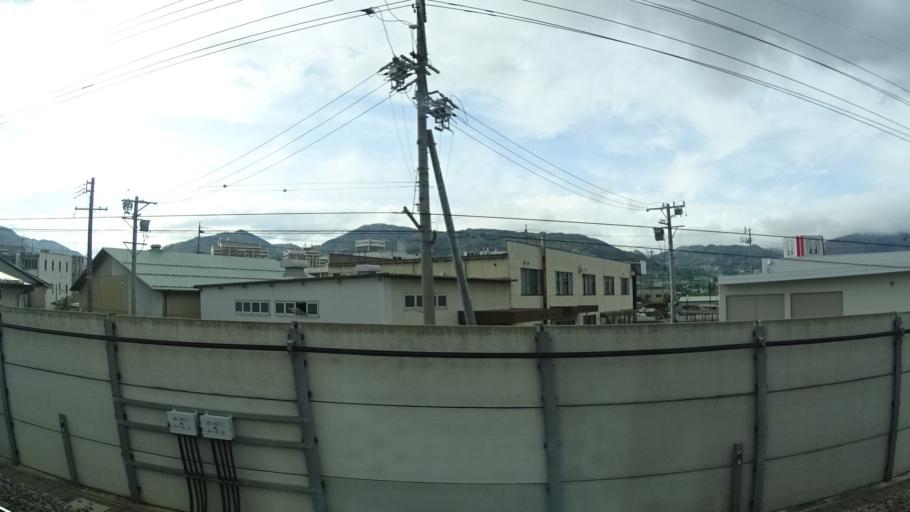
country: JP
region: Nagano
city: Nagano-shi
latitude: 36.6553
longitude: 138.2067
